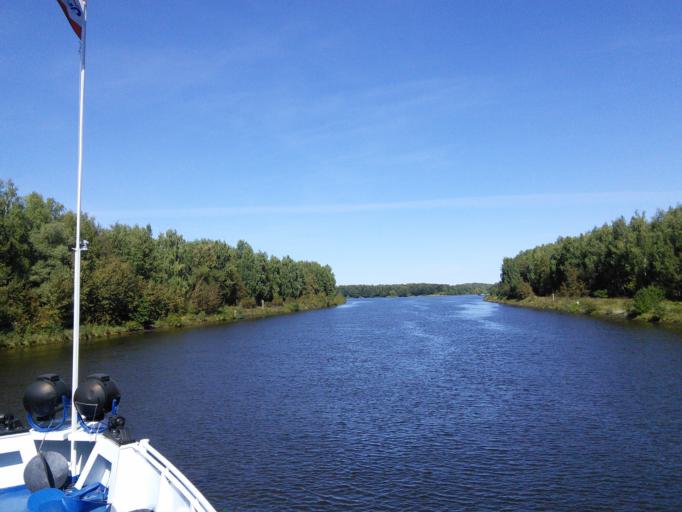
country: RU
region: Moskovskaya
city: Pirogovskiy
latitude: 56.0355
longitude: 37.6673
